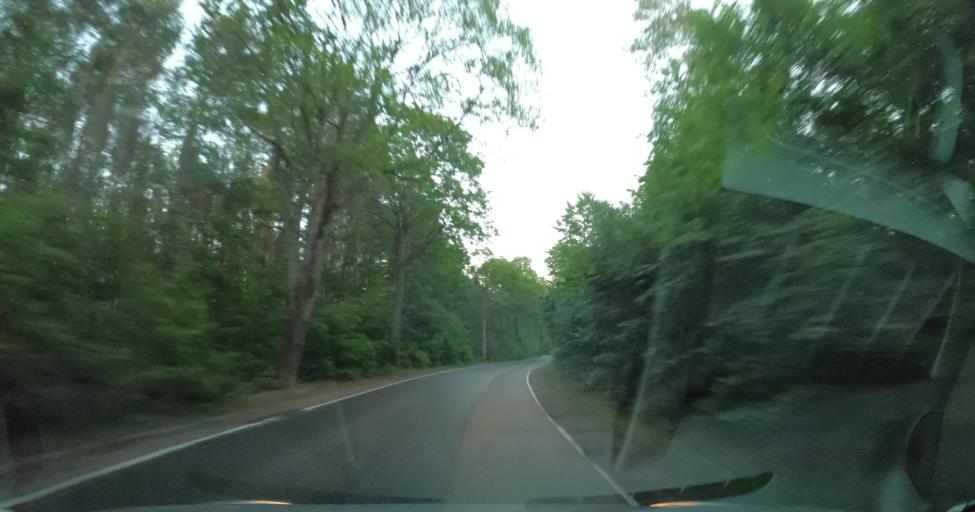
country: PL
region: Pomeranian Voivodeship
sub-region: Powiat wejherowski
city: Luzino
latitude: 54.4660
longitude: 18.1117
